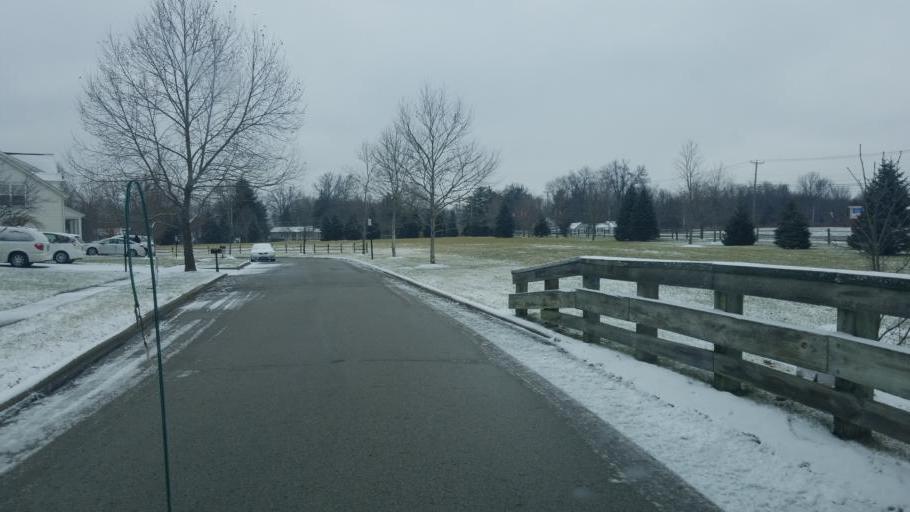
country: US
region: Ohio
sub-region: Franklin County
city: New Albany
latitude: 40.0177
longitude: -82.7906
